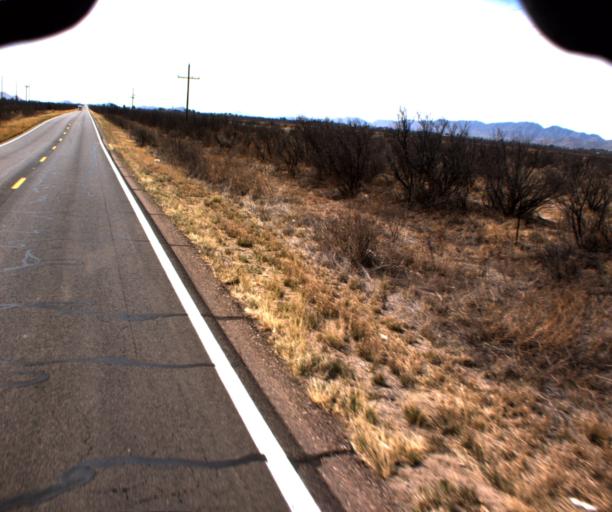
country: US
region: Arizona
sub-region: Cochise County
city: Willcox
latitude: 32.0269
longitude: -109.8744
